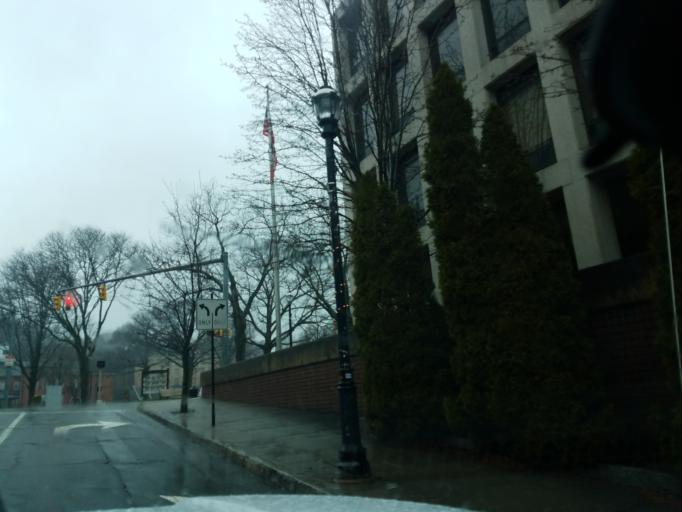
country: US
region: Connecticut
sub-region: New Haven County
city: Naugatuck
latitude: 41.4905
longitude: -73.0550
